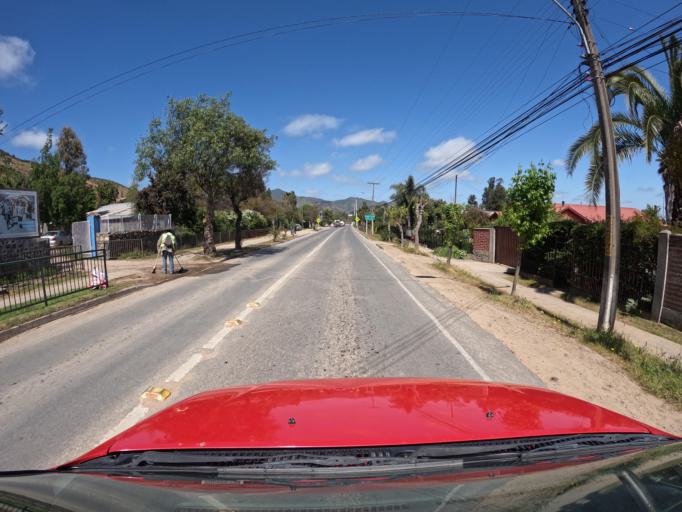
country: CL
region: O'Higgins
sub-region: Provincia de Colchagua
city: Santa Cruz
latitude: -34.7238
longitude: -71.6400
